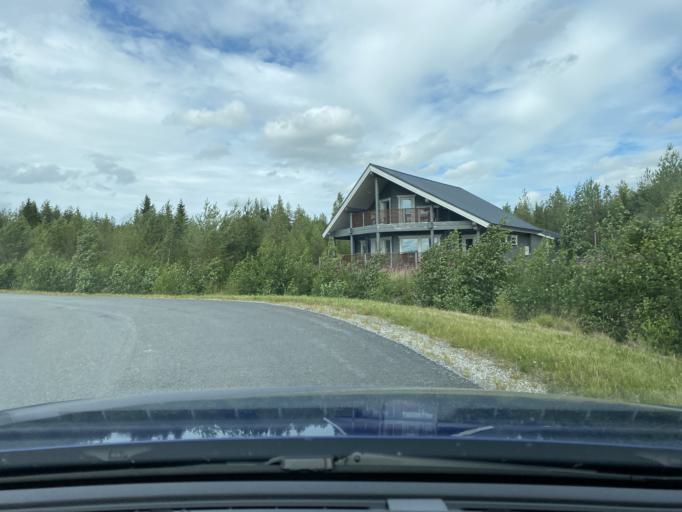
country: FI
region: Southern Ostrobothnia
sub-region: Seinaejoki
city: Jurva
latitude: 62.6247
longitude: 22.0312
